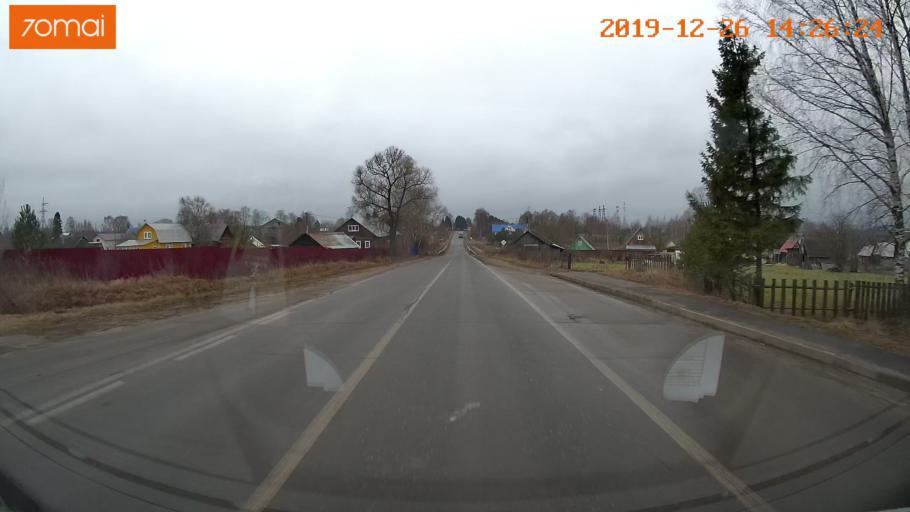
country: RU
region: Jaroslavl
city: Poshekhon'ye
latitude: 58.4864
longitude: 39.0884
